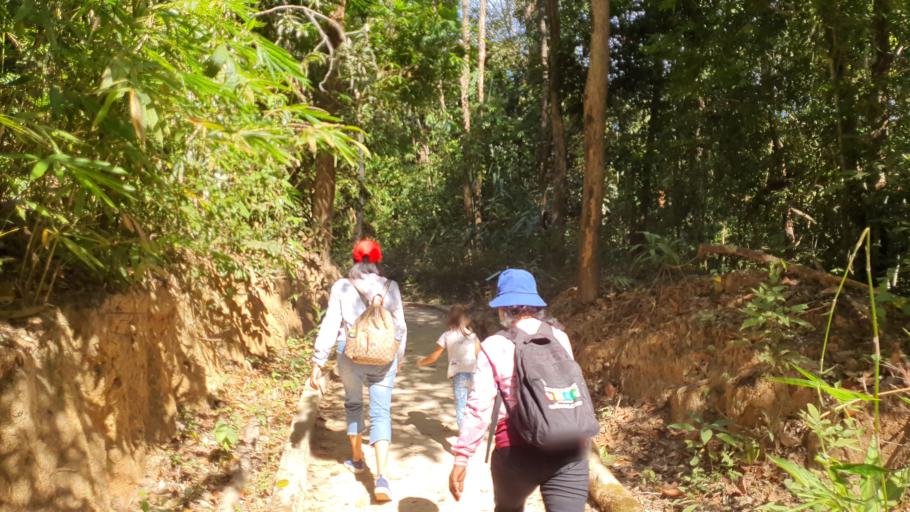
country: TH
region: Nakhon Phanom
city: Ban Phaeng
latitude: 17.9843
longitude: 104.1340
